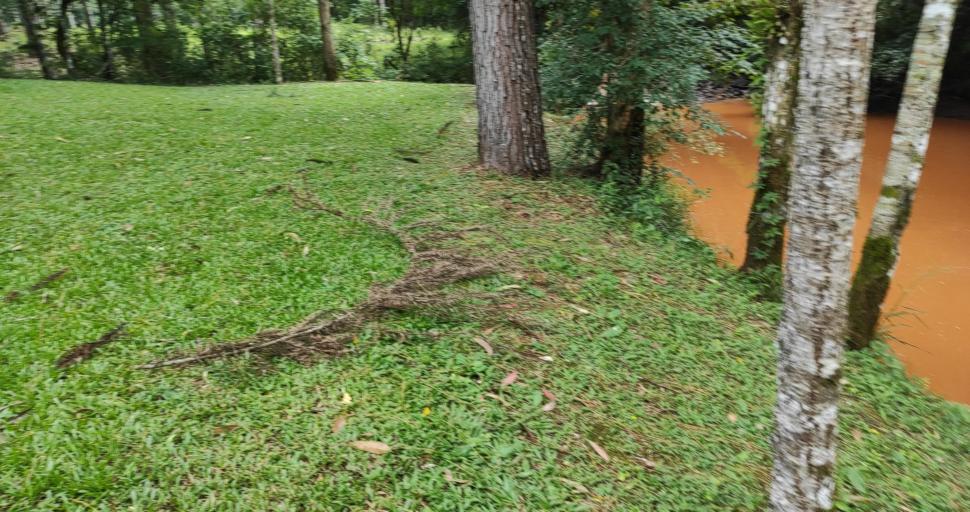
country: AR
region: Misiones
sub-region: Departamento de Veinticinco de Mayo
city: Veinticinco de Mayo
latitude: -27.4177
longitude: -54.7022
